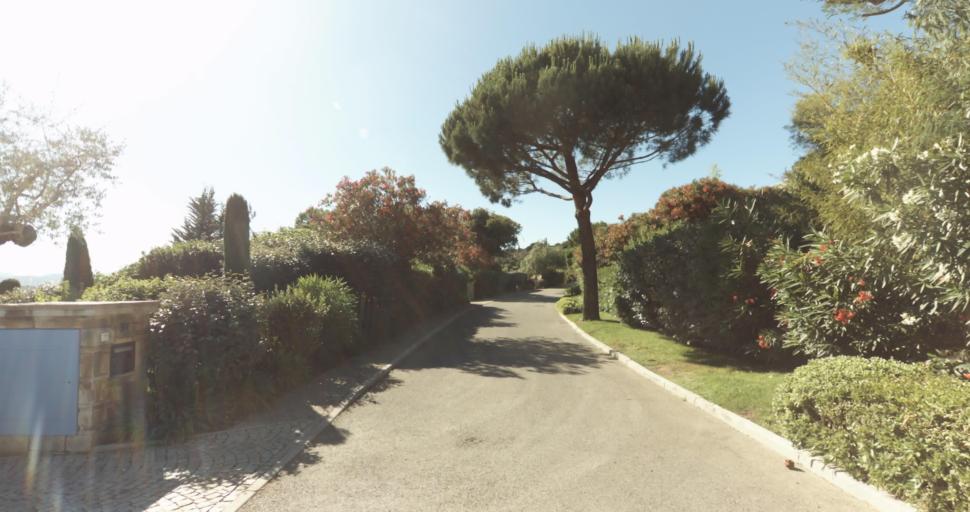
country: FR
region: Provence-Alpes-Cote d'Azur
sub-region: Departement du Var
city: Gassin
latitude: 43.2553
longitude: 6.6076
